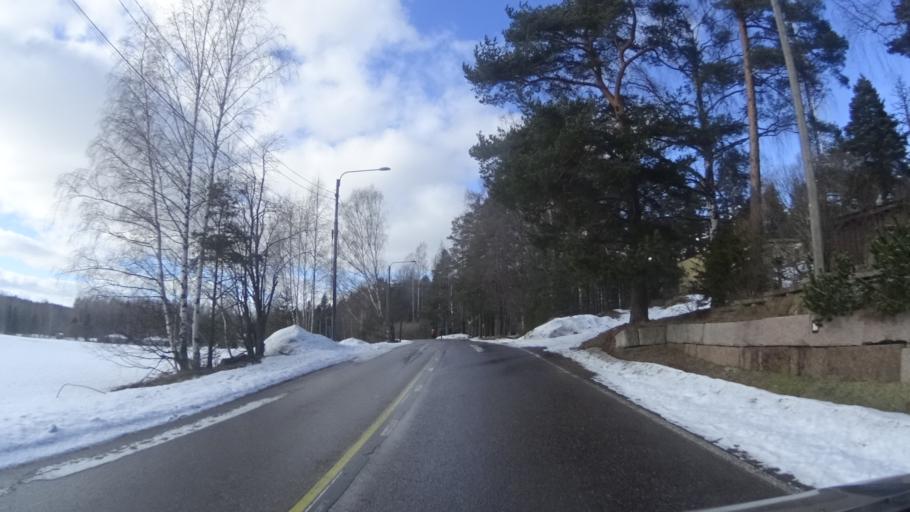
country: FI
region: Uusimaa
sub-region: Helsinki
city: Vantaa
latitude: 60.2516
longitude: 25.1720
